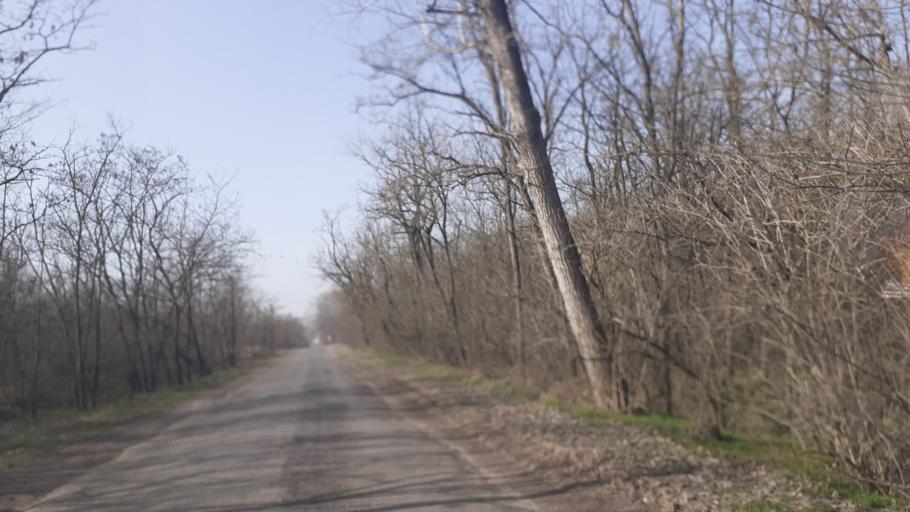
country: HU
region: Pest
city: Dabas
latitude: 47.0657
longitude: 19.2725
